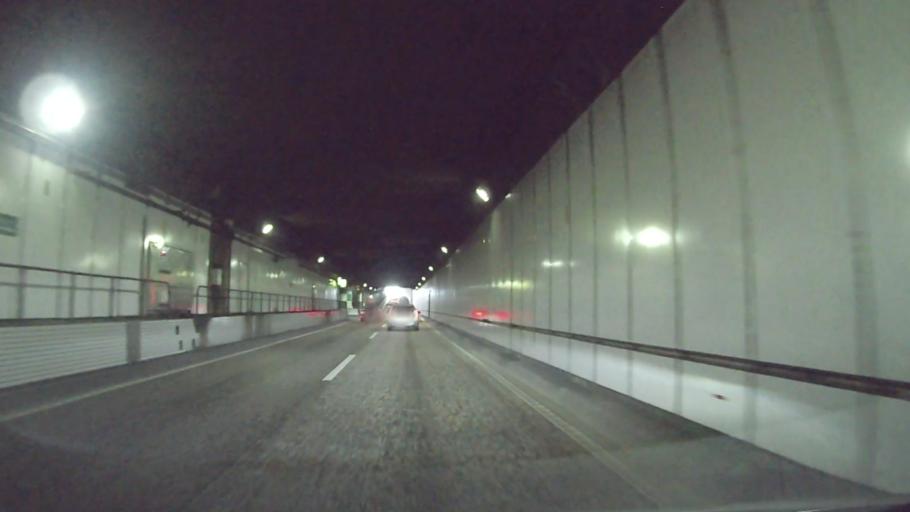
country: JP
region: Tokyo
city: Musashino
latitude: 35.7221
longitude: 139.6145
